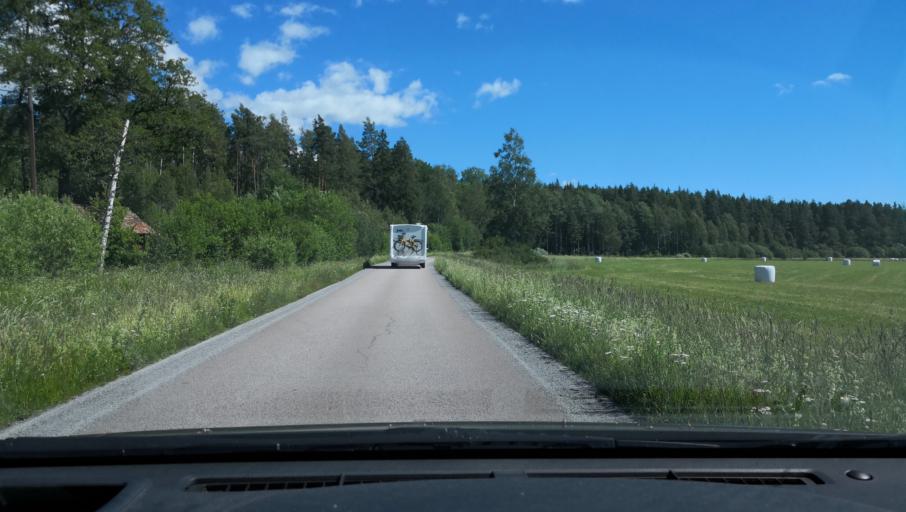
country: SE
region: Vaestmanland
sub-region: Arboga Kommun
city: Tyringe
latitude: 59.3932
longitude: 15.9392
